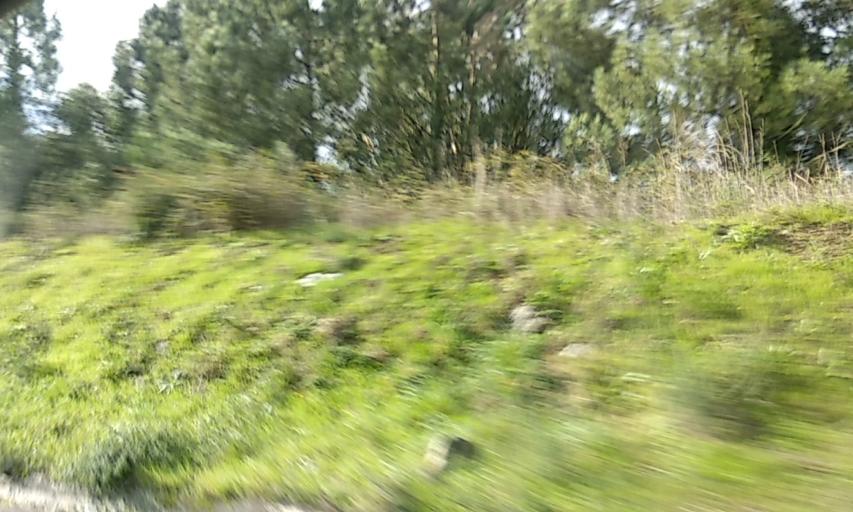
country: PT
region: Braga
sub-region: Braga
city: Oliveira
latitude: 41.4857
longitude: -8.4665
